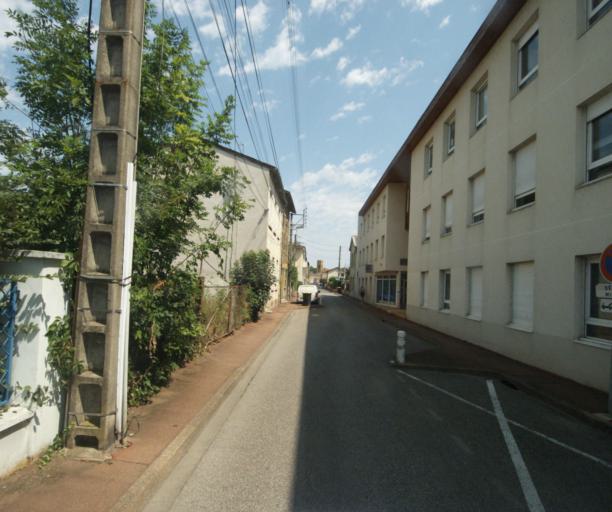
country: FR
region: Rhone-Alpes
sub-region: Departement du Rhone
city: Saint-Germain-Nuelles
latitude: 45.8309
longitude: 4.6139
